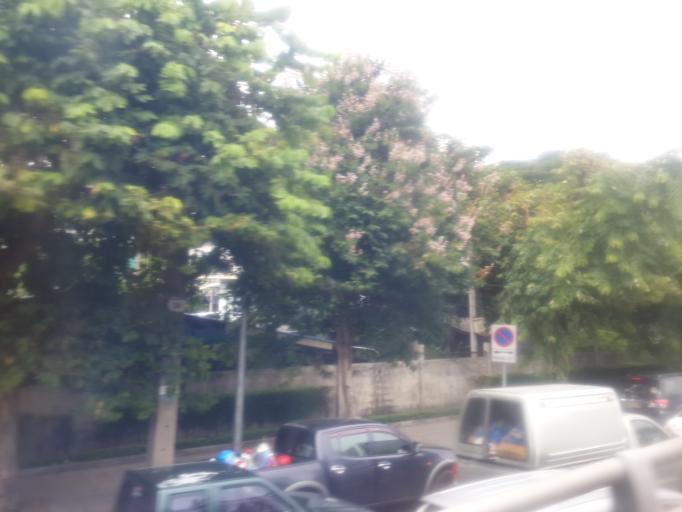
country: TH
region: Bangkok
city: Pom Prap Sattru Phai
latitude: 13.7582
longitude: 100.5195
